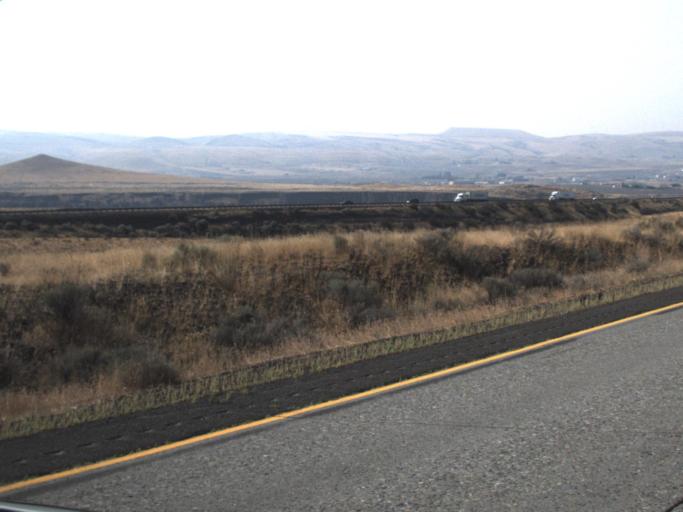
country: US
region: Washington
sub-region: Yakima County
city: Terrace Heights
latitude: 46.7094
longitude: -120.4353
